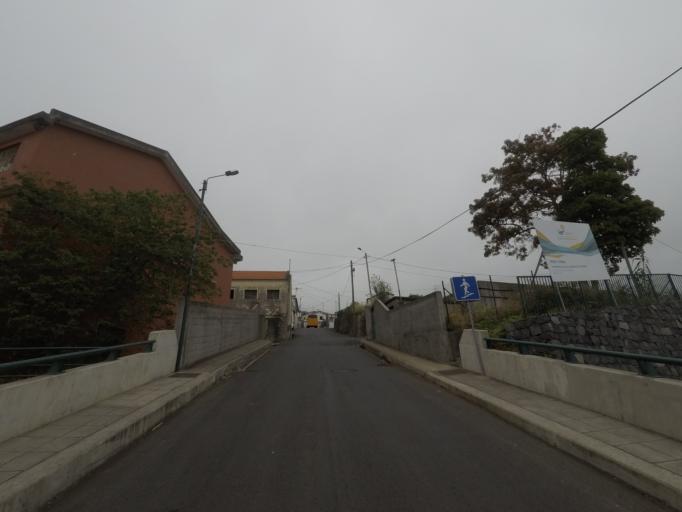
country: PT
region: Madeira
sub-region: Funchal
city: Nossa Senhora do Monte
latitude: 32.6782
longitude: -16.9464
